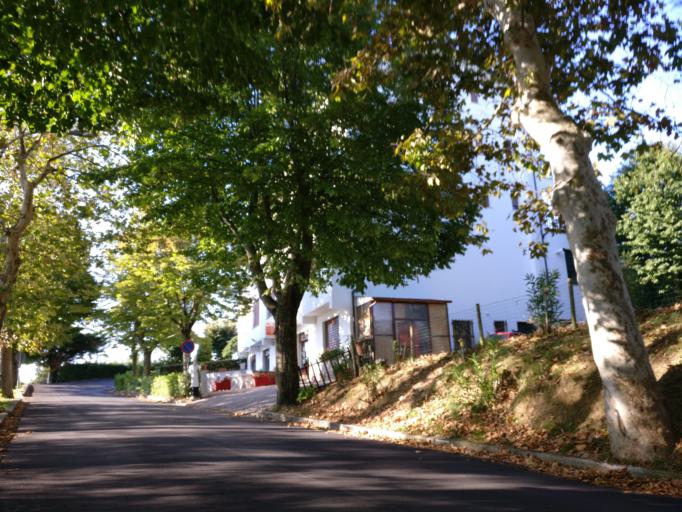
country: IT
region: The Marches
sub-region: Provincia di Ascoli Piceno
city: Montedinove
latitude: 42.9724
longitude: 13.5907
